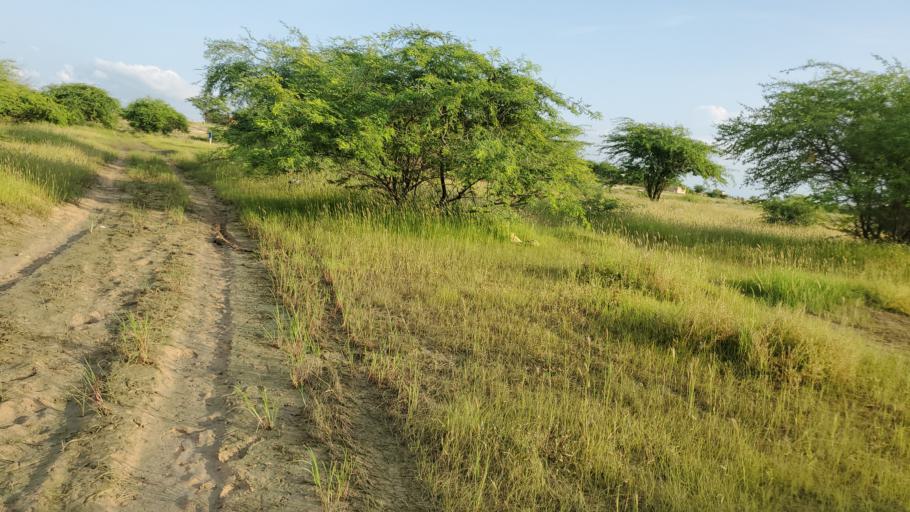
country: SN
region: Saint-Louis
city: Saint-Louis
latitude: 16.0501
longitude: -16.4198
